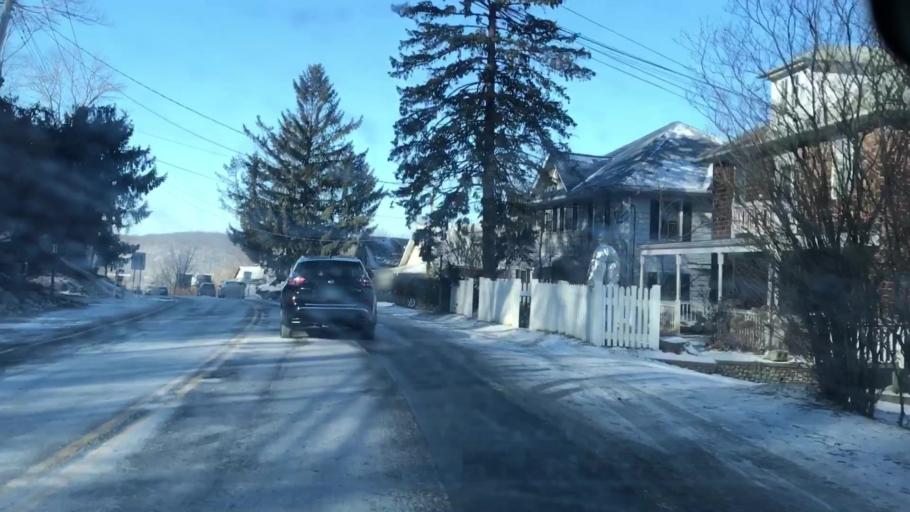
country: US
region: New York
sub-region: Putnam County
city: Brewster
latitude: 41.3995
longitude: -73.6266
